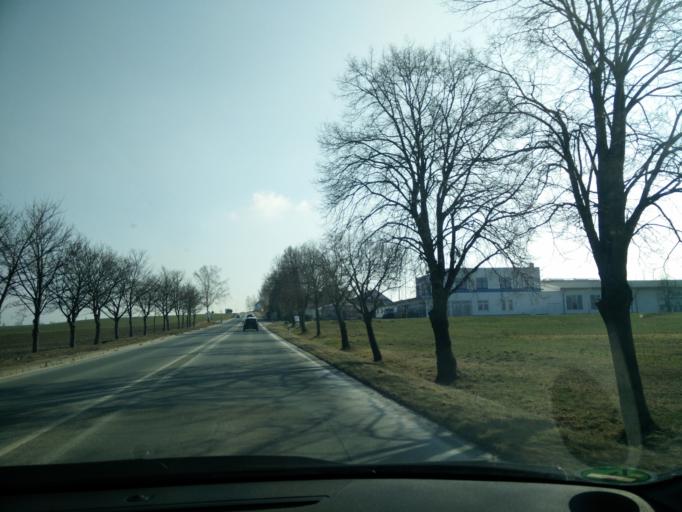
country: DE
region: Saxony
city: Niederfrohna
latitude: 50.9192
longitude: 12.7186
